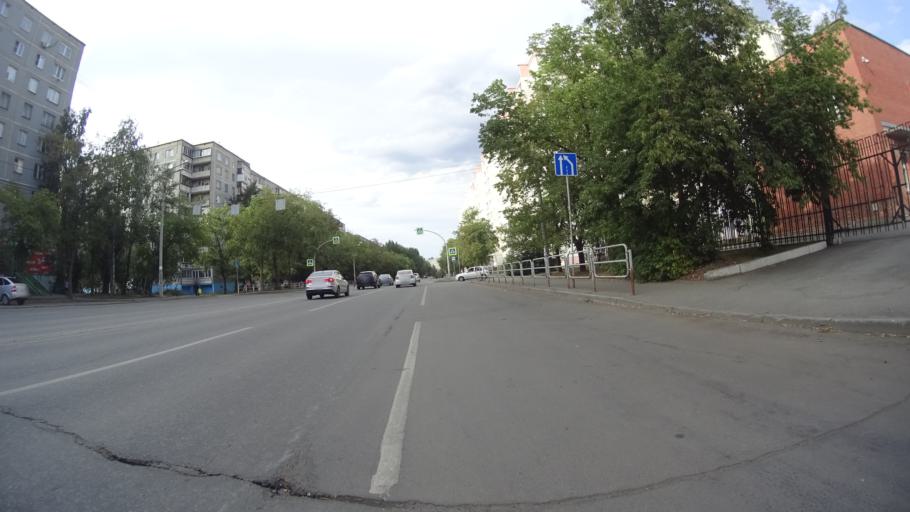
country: RU
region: Chelyabinsk
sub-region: Gorod Chelyabinsk
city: Chelyabinsk
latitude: 55.1953
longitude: 61.3179
